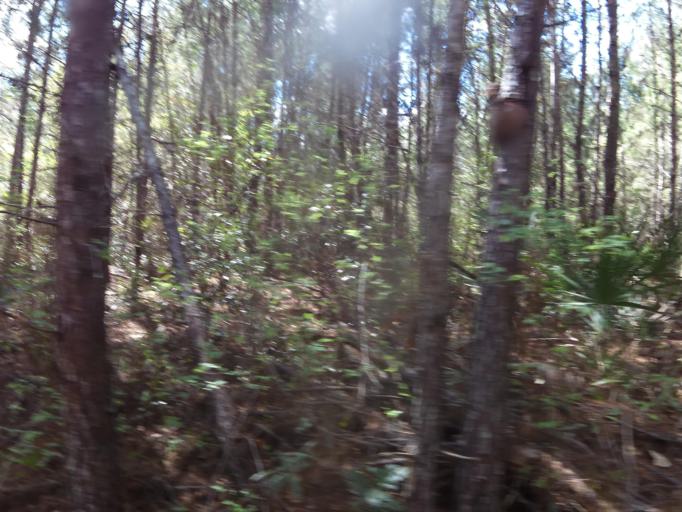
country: US
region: Florida
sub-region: Putnam County
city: Interlachen
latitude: 29.7643
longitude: -81.8584
